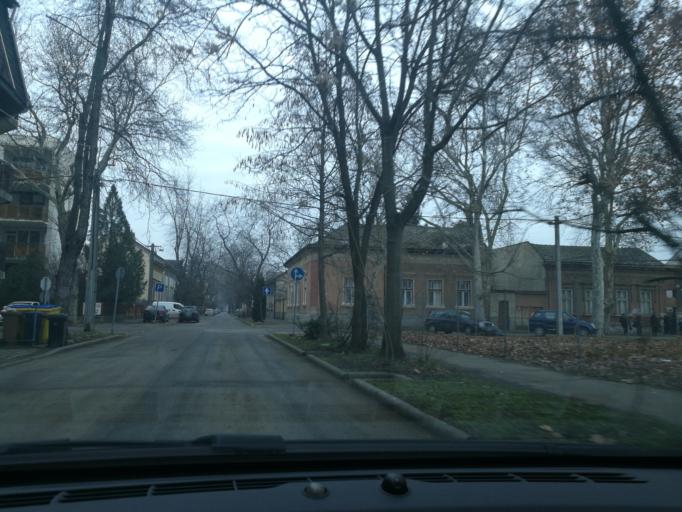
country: HU
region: Szabolcs-Szatmar-Bereg
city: Nyiregyhaza
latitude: 47.9489
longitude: 21.7112
